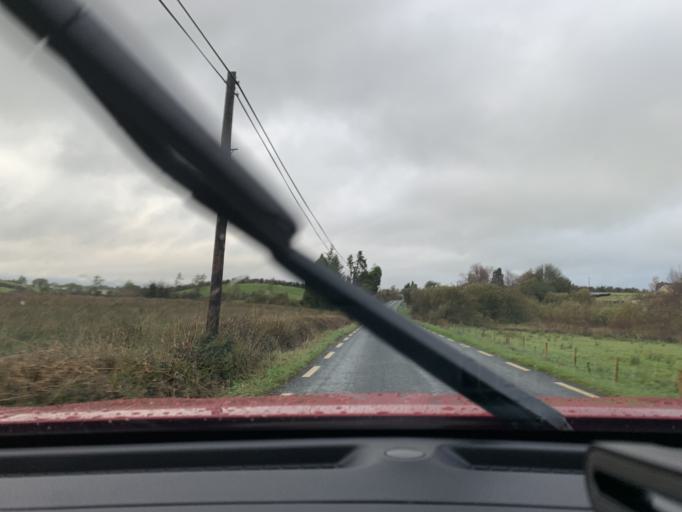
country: IE
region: Connaught
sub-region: Sligo
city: Ballymote
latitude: 54.0354
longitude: -8.5211
